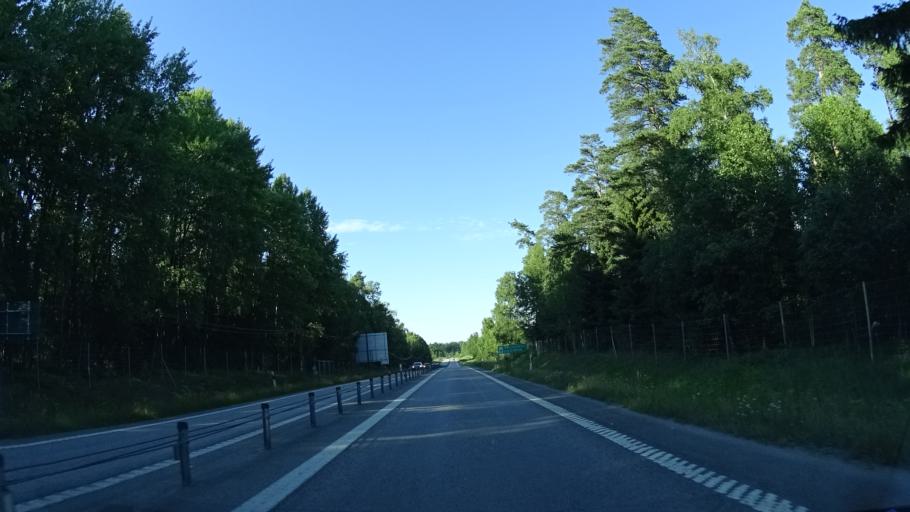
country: SE
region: Stockholm
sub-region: Vallentuna Kommun
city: Vallentuna
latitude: 59.5032
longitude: 18.1695
